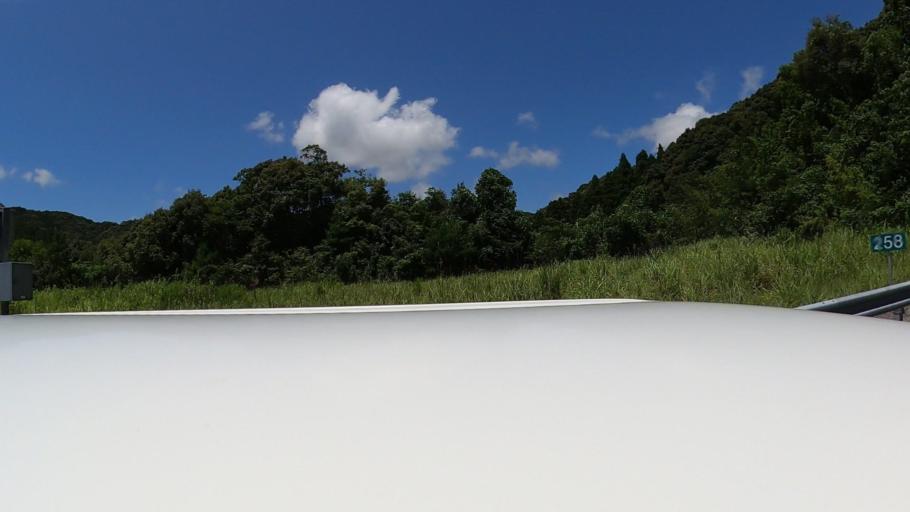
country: JP
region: Miyazaki
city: Nobeoka
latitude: 32.4808
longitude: 131.6336
